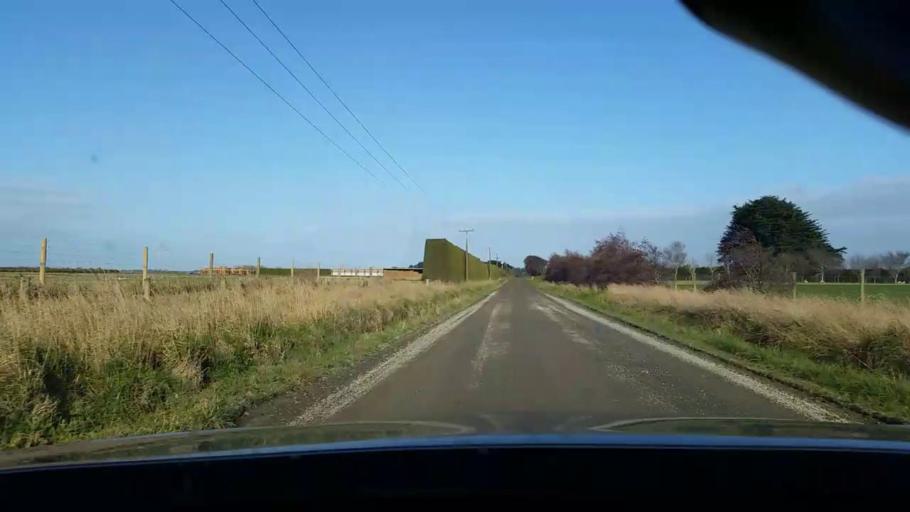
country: NZ
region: Southland
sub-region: Invercargill City
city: Invercargill
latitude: -46.3001
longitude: 168.3033
